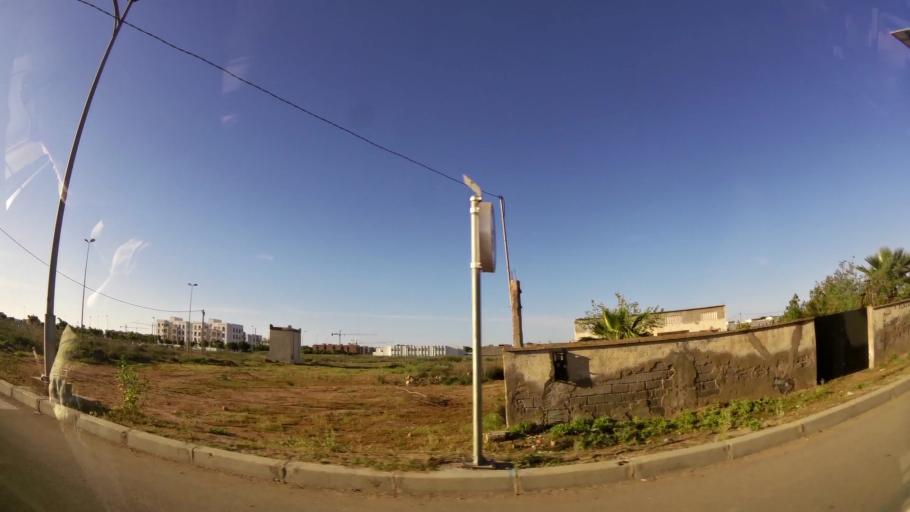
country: MA
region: Oriental
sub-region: Berkane-Taourirt
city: Madagh
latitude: 35.0829
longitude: -2.2528
